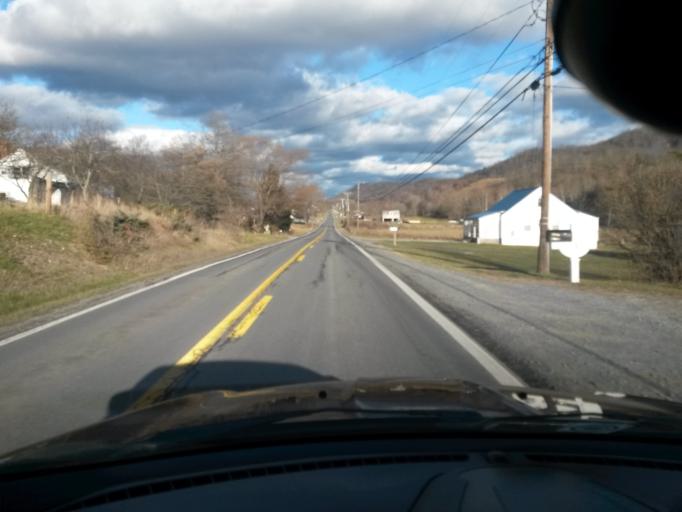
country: US
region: Virginia
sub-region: Giles County
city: Pearisburg
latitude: 37.4414
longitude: -80.6900
